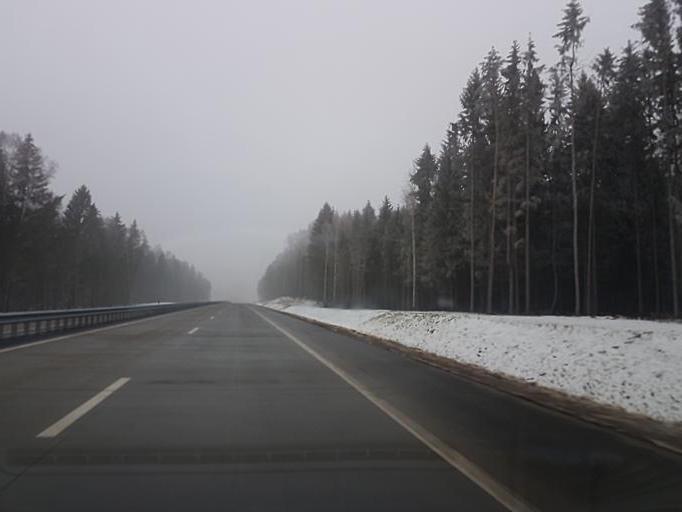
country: BY
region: Minsk
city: Atolina
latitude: 53.7197
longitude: 27.4317
